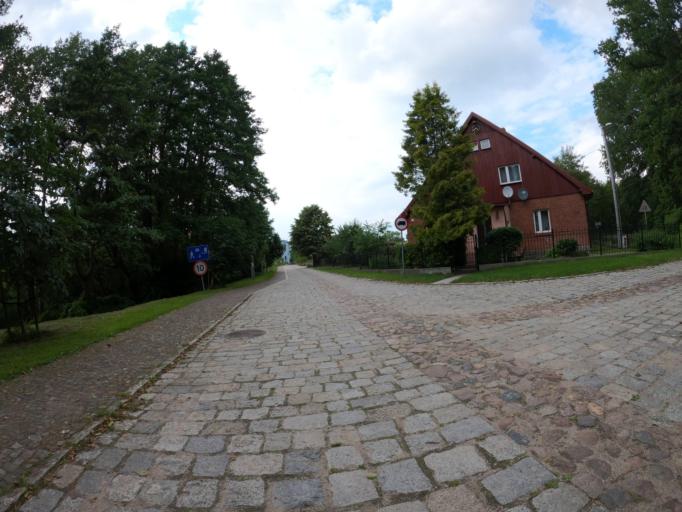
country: PL
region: West Pomeranian Voivodeship
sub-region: Powiat szczecinecki
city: Borne Sulinowo
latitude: 53.6761
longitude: 16.4920
